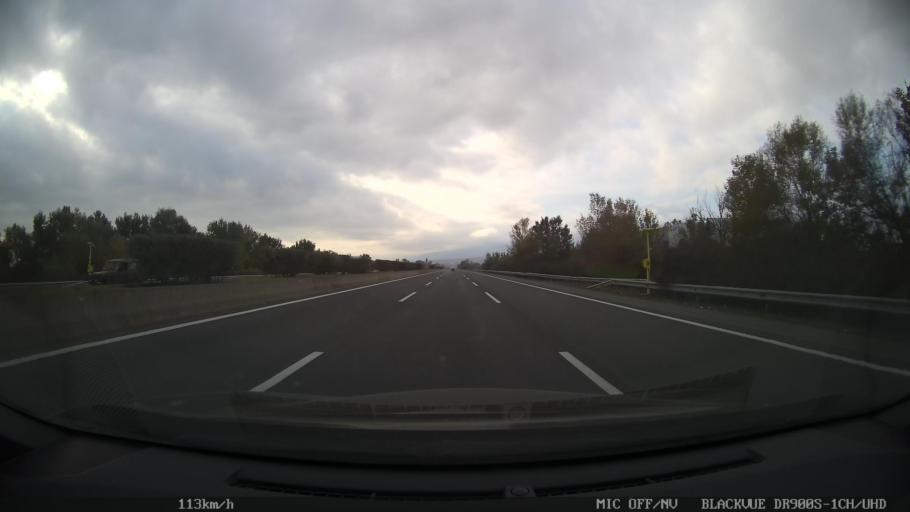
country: GR
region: Central Macedonia
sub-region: Nomos Pierias
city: Dion
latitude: 40.1751
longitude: 22.5490
